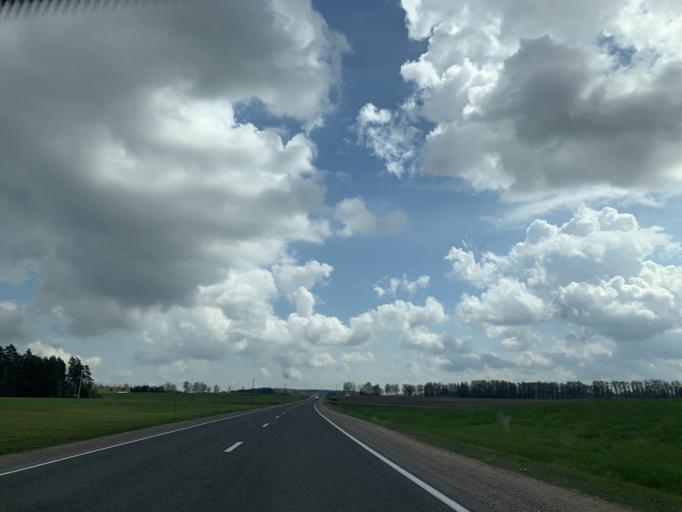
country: BY
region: Minsk
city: Nyasvizh
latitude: 53.2515
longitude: 26.6655
